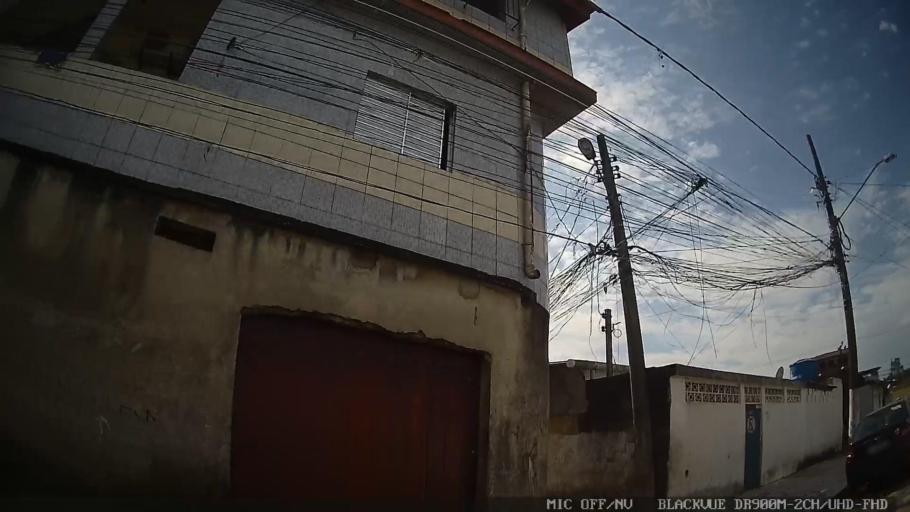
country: BR
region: Sao Paulo
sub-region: Santos
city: Santos
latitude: -23.9424
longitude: -46.2870
